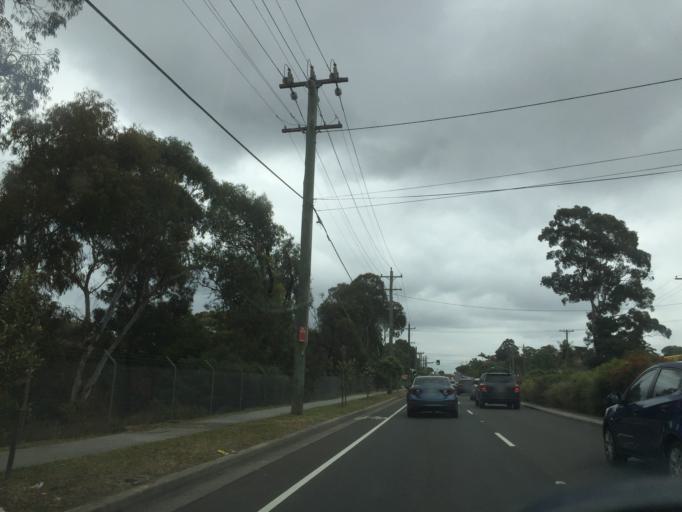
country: AU
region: New South Wales
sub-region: Holroyd
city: Girraween
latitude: -33.7671
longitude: 150.9506
